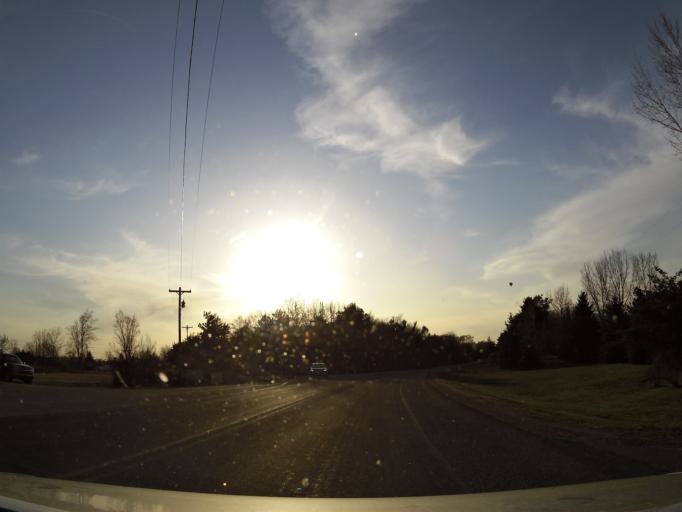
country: US
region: Minnesota
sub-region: Washington County
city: Lake Saint Croix Beach
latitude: 44.9310
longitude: -92.7089
